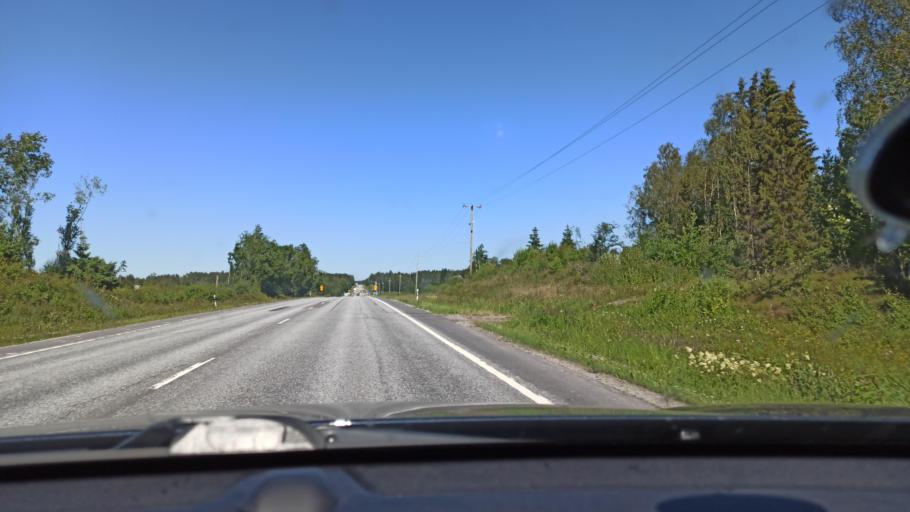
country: FI
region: Ostrobothnia
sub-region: Vaasa
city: Voera
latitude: 63.2345
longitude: 22.2506
